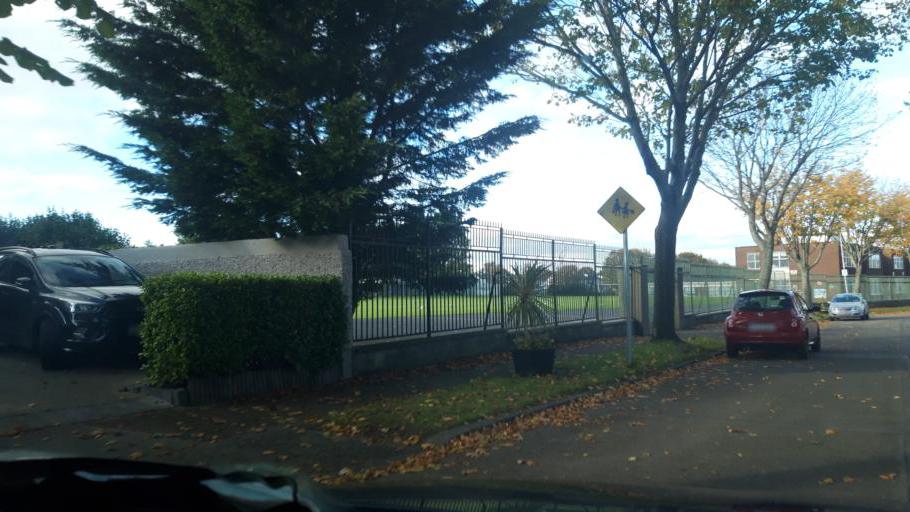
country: IE
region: Leinster
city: Raheny
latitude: 53.3935
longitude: -6.1836
